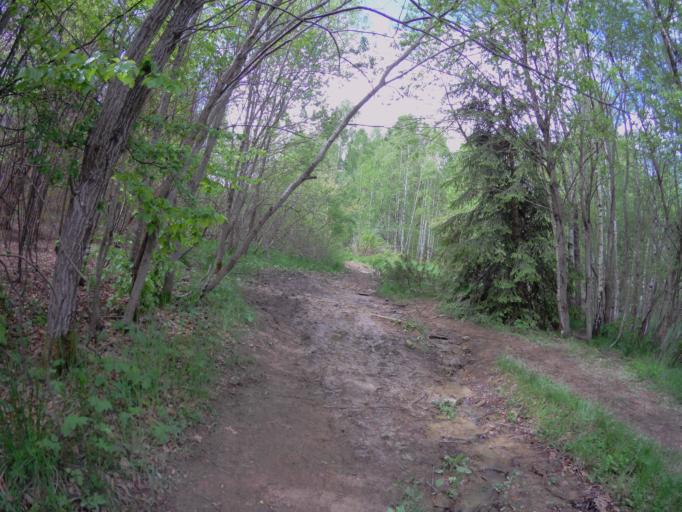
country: PL
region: Subcarpathian Voivodeship
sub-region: Powiat bieszczadzki
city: Lutowiska
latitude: 49.1435
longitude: 22.5657
